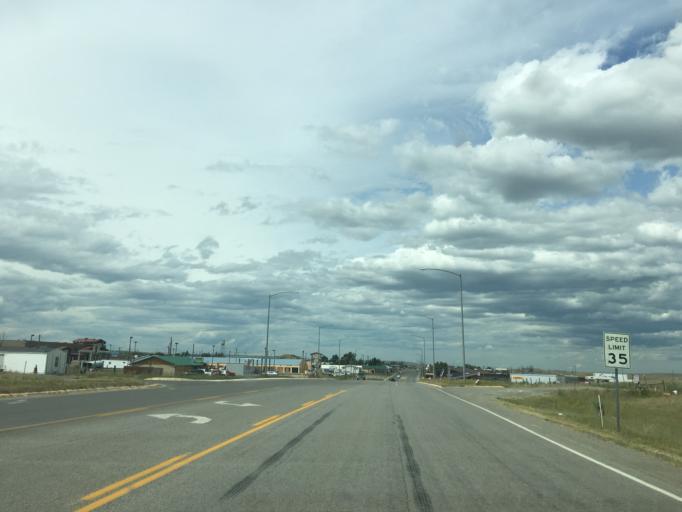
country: US
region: Montana
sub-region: Glacier County
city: South Browning
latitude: 48.5472
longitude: -113.0097
